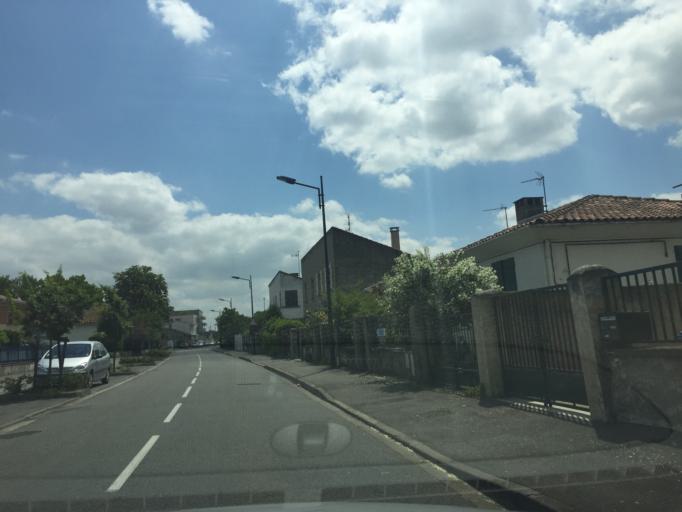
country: FR
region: Midi-Pyrenees
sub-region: Departement de la Haute-Garonne
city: Aucamville
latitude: 43.6414
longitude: 1.4445
